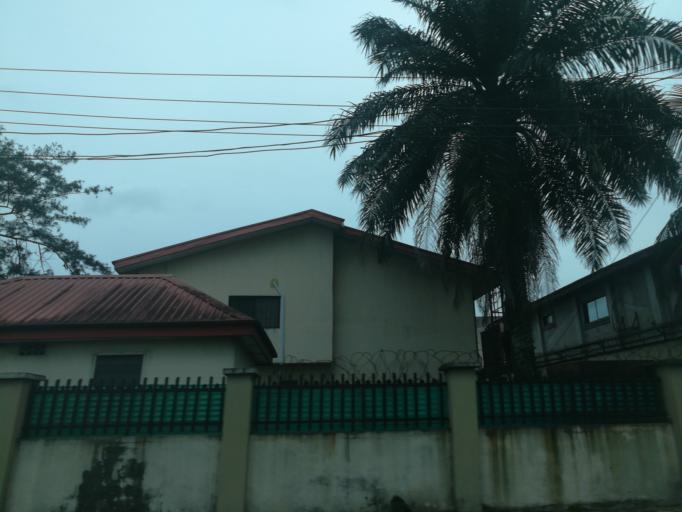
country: NG
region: Rivers
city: Port Harcourt
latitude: 4.8175
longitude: 6.9981
